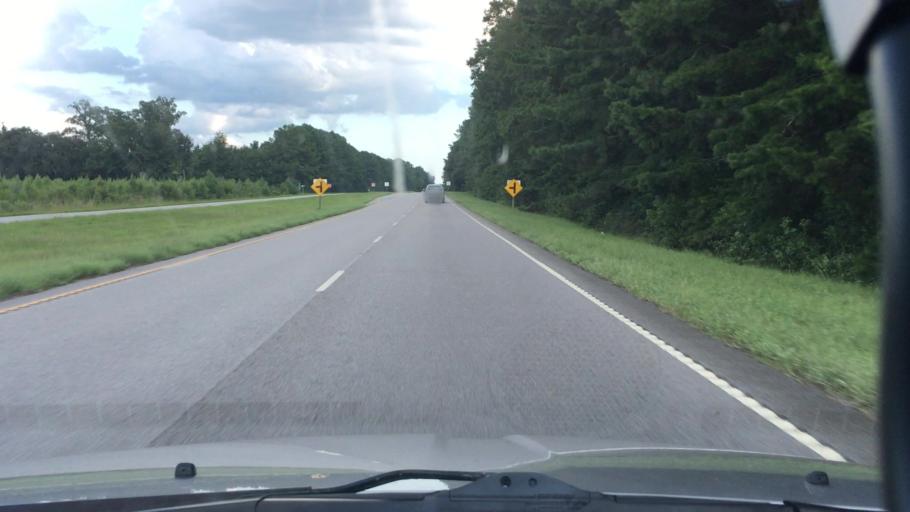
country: US
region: South Carolina
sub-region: Hampton County
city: Yemassee
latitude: 32.6304
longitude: -80.8346
